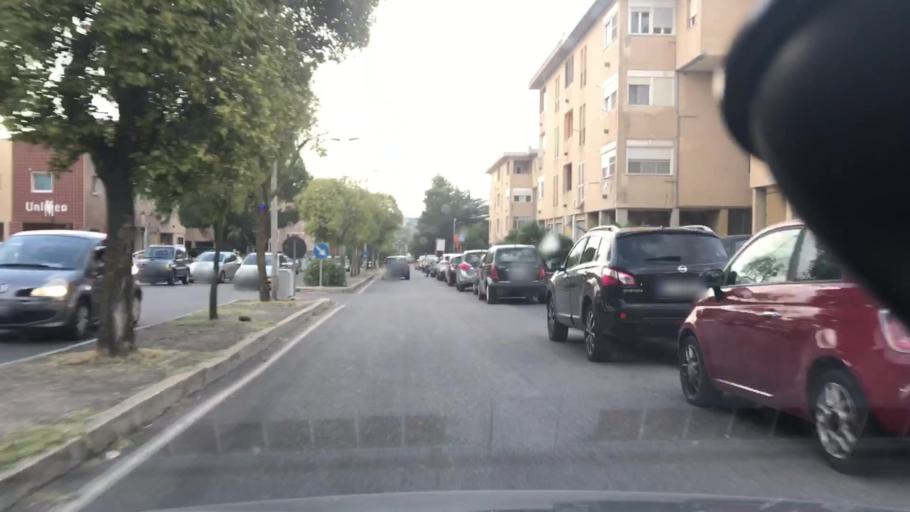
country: IT
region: Basilicate
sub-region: Provincia di Matera
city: Matera
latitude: 40.6834
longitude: 16.5851
